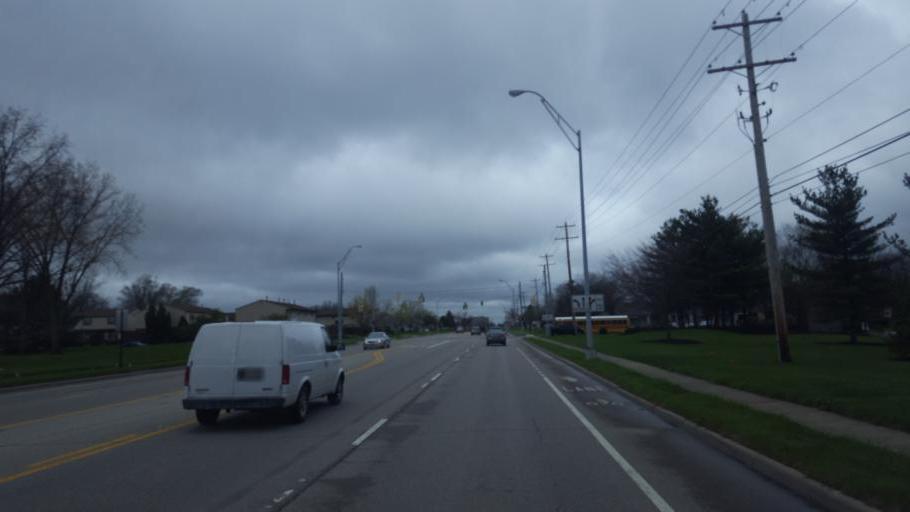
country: US
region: Ohio
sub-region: Franklin County
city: Minerva Park
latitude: 40.1066
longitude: -82.9685
